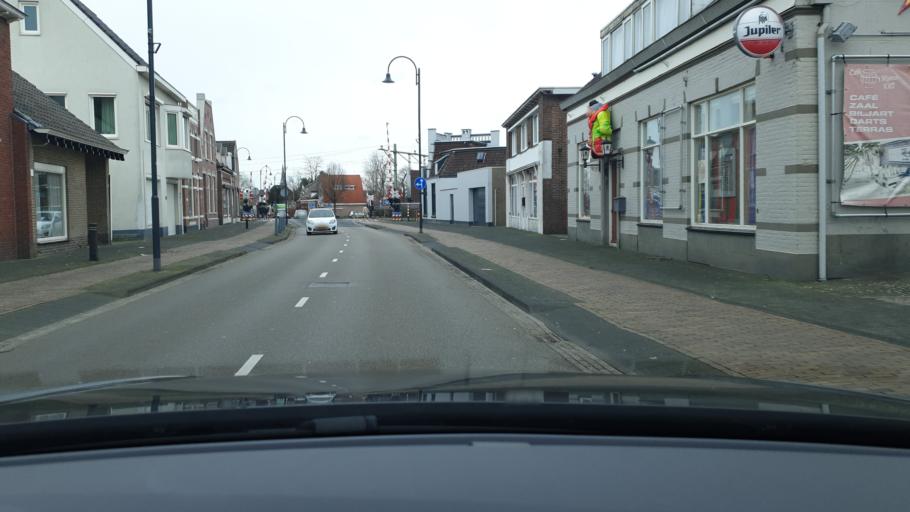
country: NL
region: North Brabant
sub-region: Gemeente Dongen
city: Dongen
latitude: 51.5833
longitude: 4.9238
